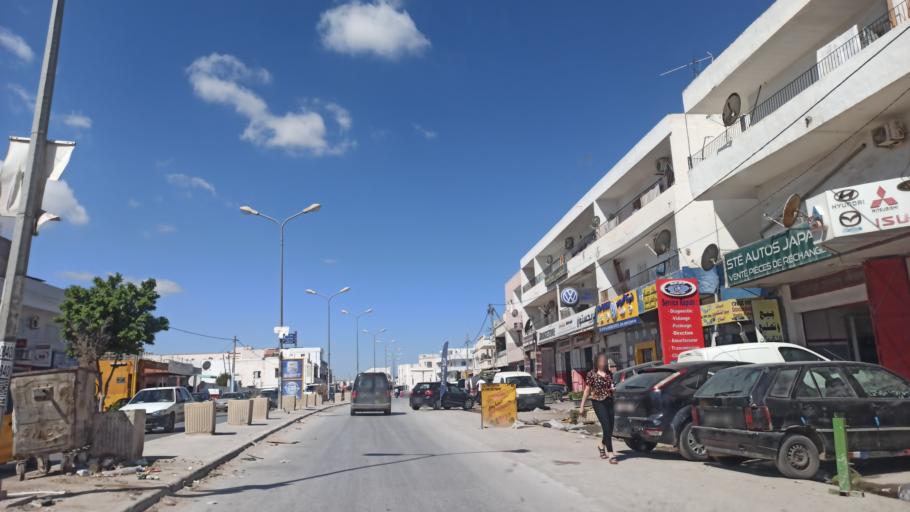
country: TN
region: Manouba
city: Manouba
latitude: 36.7984
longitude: 10.1047
